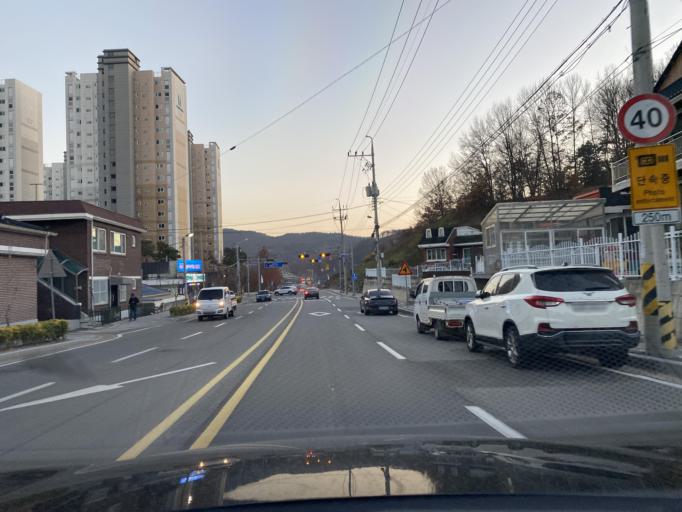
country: KR
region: Chungcheongnam-do
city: Yesan
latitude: 36.6837
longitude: 126.8437
